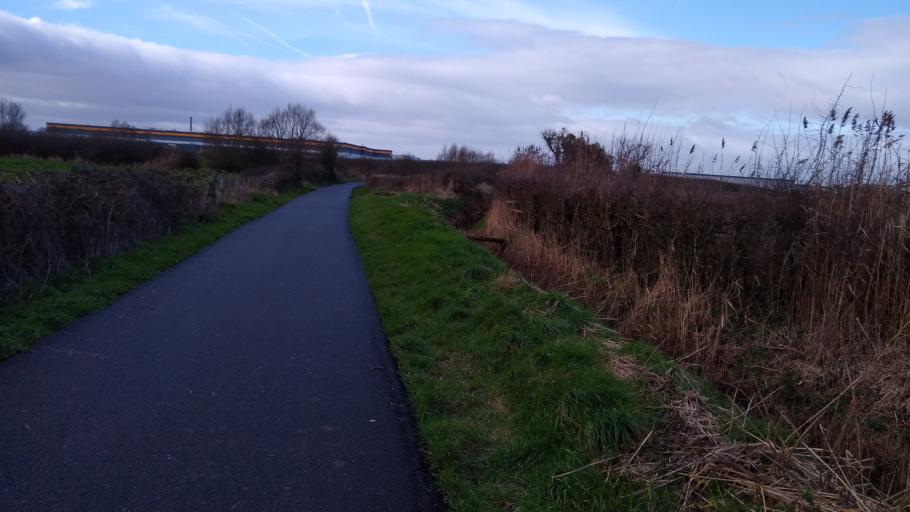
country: GB
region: England
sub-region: South Gloucestershire
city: Severn Beach
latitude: 51.5411
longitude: -2.6306
